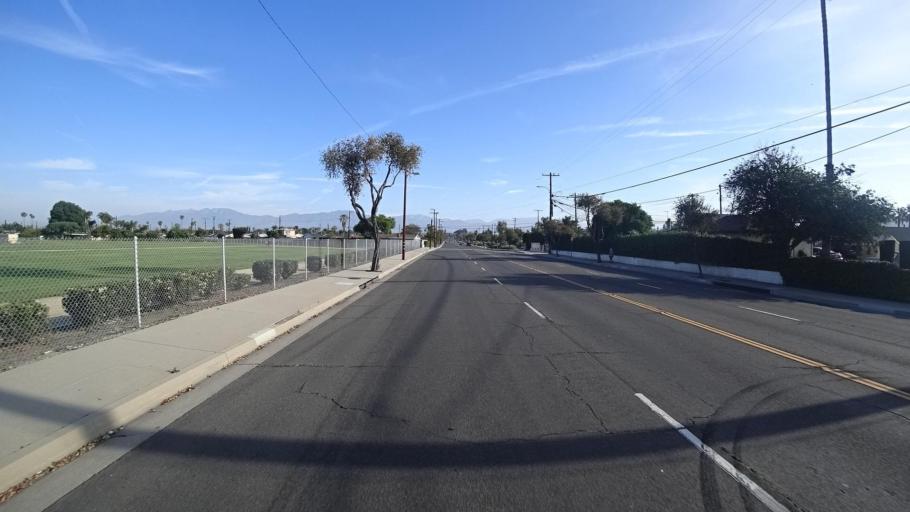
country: US
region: California
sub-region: Los Angeles County
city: Valinda
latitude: 34.0293
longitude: -117.9270
